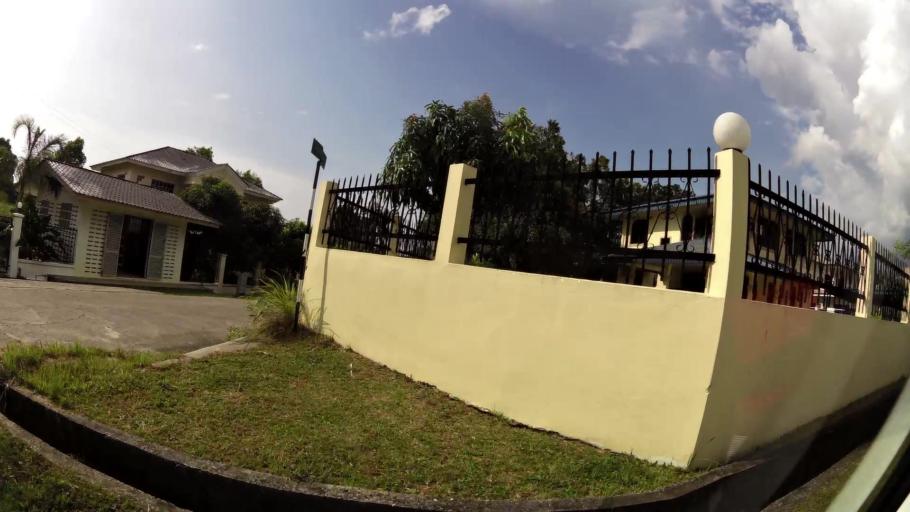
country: BN
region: Brunei and Muara
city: Bandar Seri Begawan
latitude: 4.9605
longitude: 114.9701
